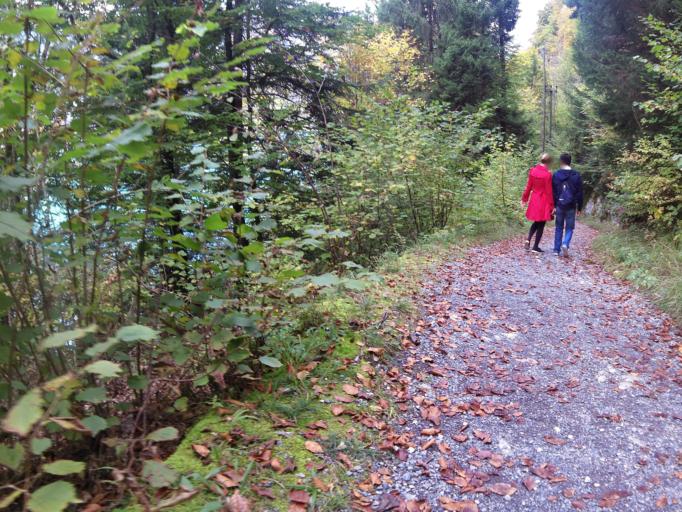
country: CH
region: Bern
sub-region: Interlaken-Oberhasli District
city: Brienz
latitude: 46.7354
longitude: 8.0212
